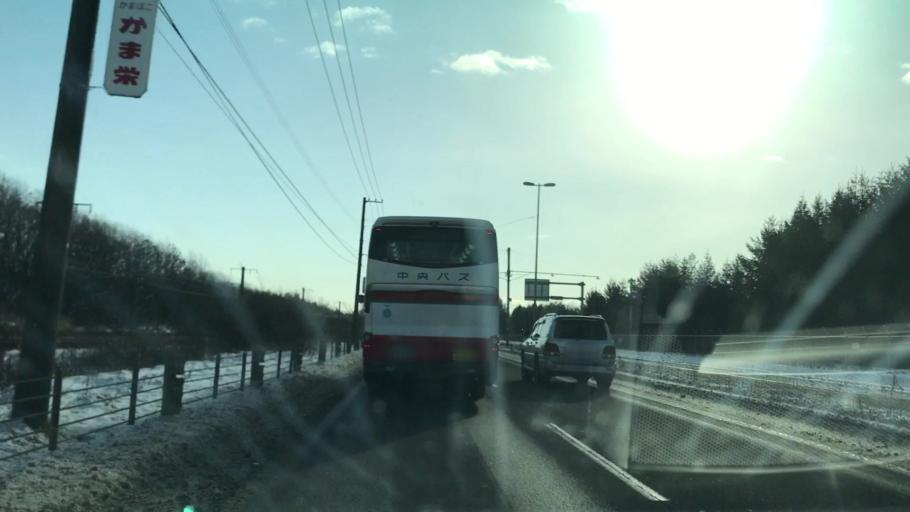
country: JP
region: Hokkaido
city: Chitose
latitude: 42.8173
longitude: 141.6641
